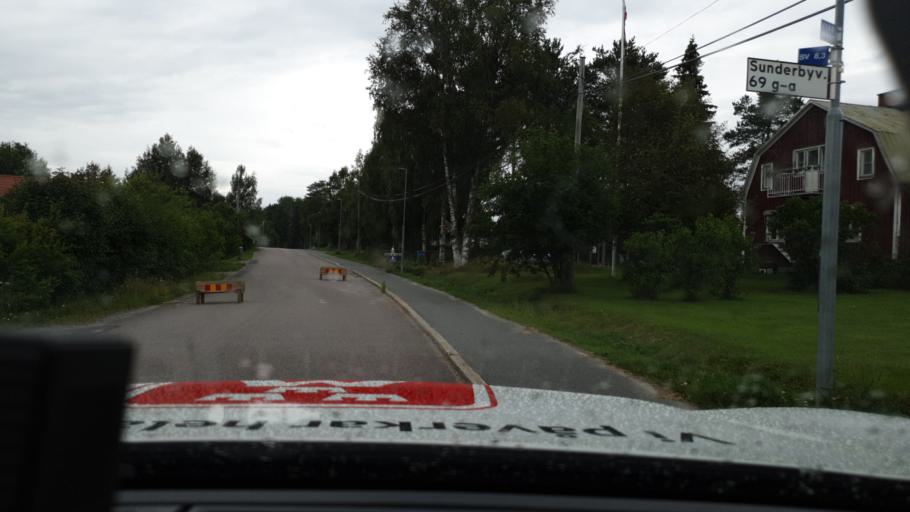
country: SE
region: Norrbotten
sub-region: Lulea Kommun
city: Sodra Sunderbyn
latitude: 65.6650
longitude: 21.9228
